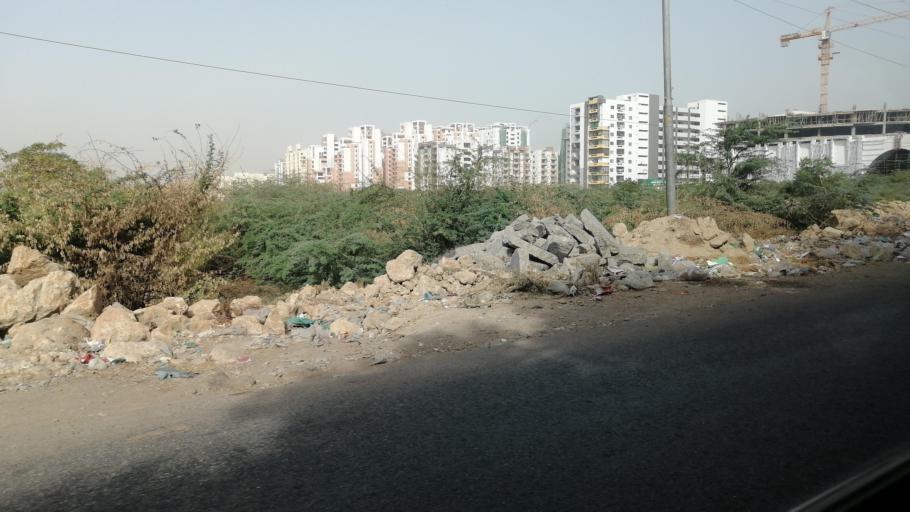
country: PK
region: Sindh
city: Malir Cantonment
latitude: 24.9245
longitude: 67.1805
